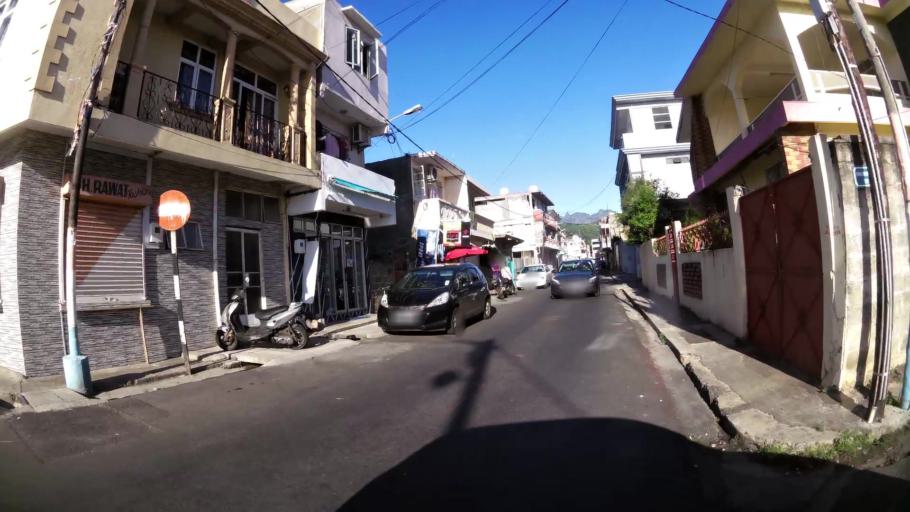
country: MU
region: Port Louis
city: Port Louis
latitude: -20.1530
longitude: 57.5089
